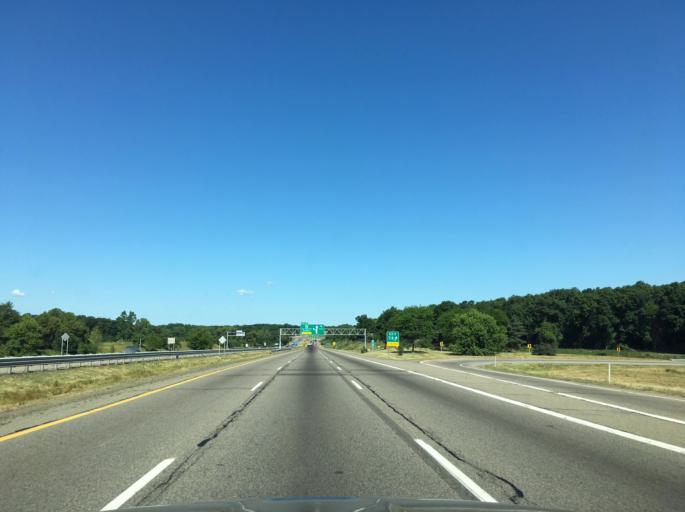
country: US
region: Michigan
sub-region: Oakland County
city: Bloomfield Hills
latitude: 42.6072
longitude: -83.2104
